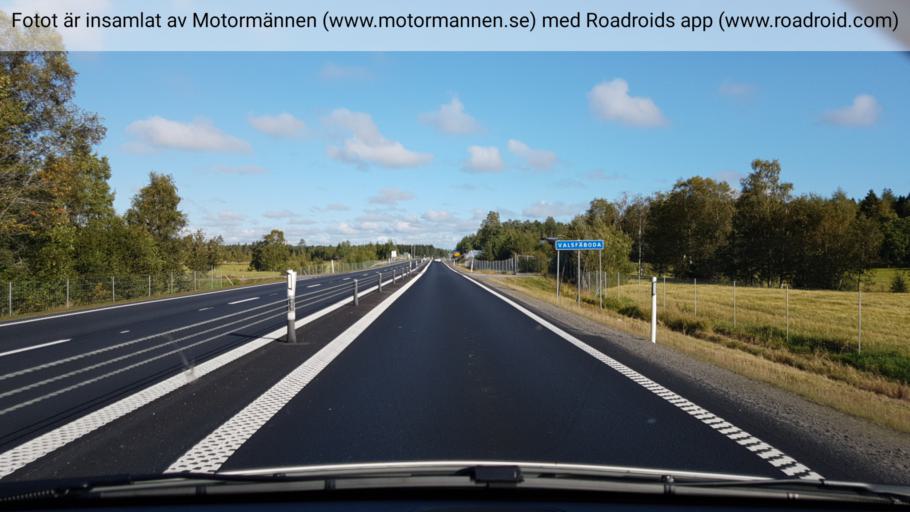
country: SE
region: Vaesterbotten
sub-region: Robertsfors Kommun
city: Robertsfors
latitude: 64.1142
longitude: 20.8805
